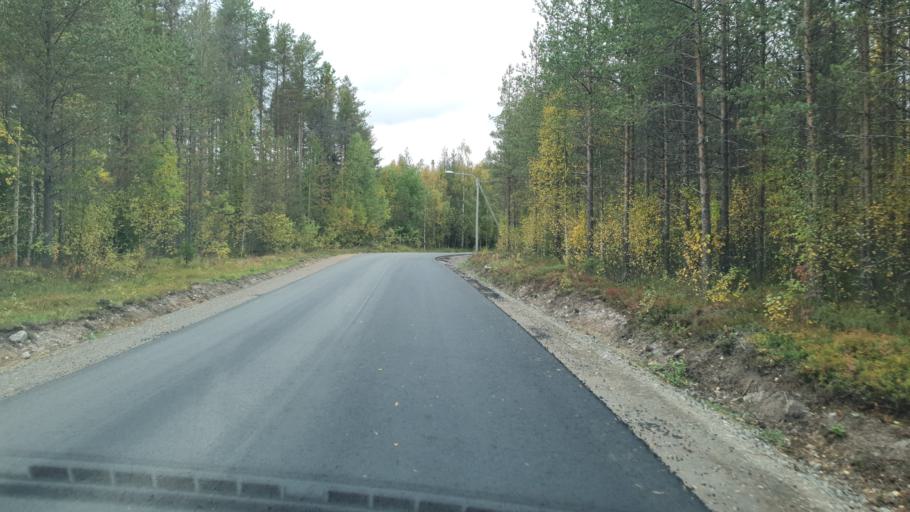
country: FI
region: Lapland
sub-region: Rovaniemi
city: Rovaniemi
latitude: 66.4243
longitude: 25.4009
